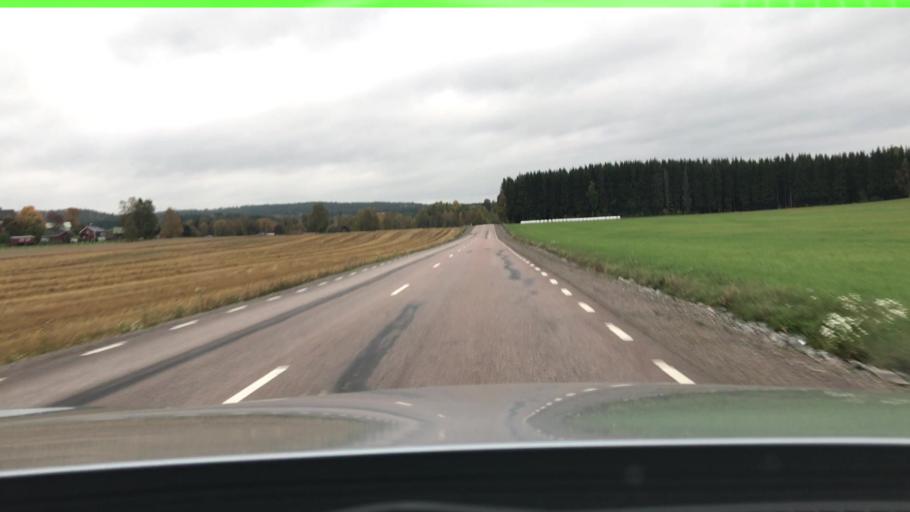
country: SE
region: Vaermland
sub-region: Eda Kommun
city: Amotfors
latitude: 59.7356
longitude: 12.1982
